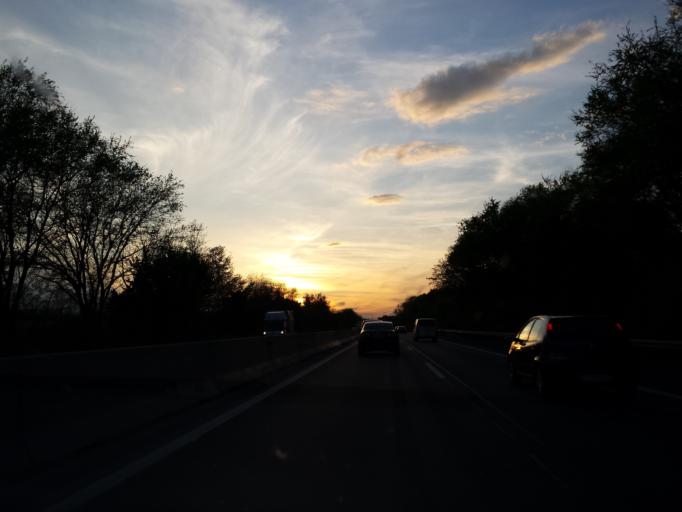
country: AT
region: Lower Austria
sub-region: Politischer Bezirk Bruck an der Leitha
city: Bruck an der Leitha
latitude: 48.0531
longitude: 16.7260
